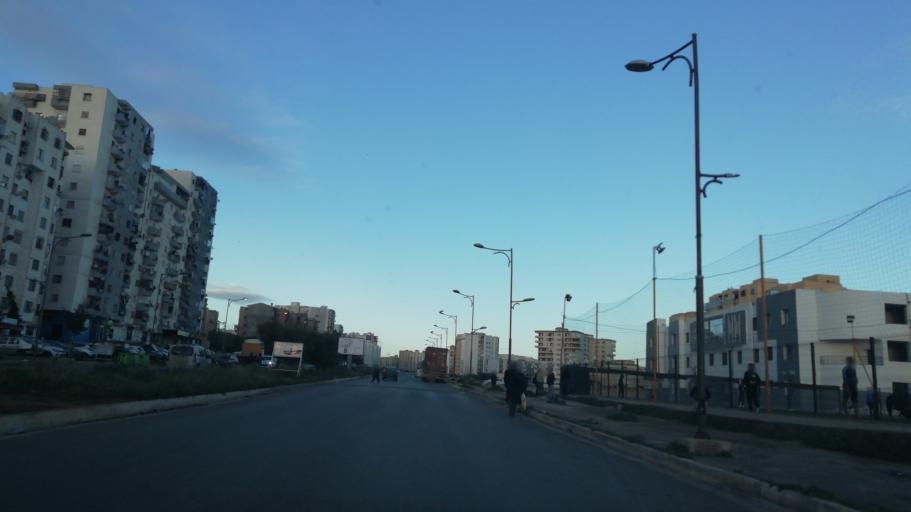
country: DZ
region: Oran
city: Bir el Djir
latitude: 35.6943
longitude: -0.5689
